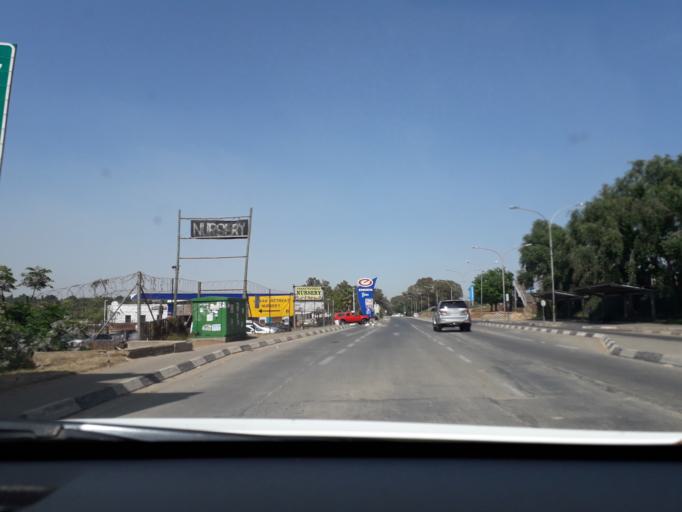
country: ZA
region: Gauteng
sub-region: Ekurhuleni Metropolitan Municipality
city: Tembisa
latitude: -26.0668
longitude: 28.2355
